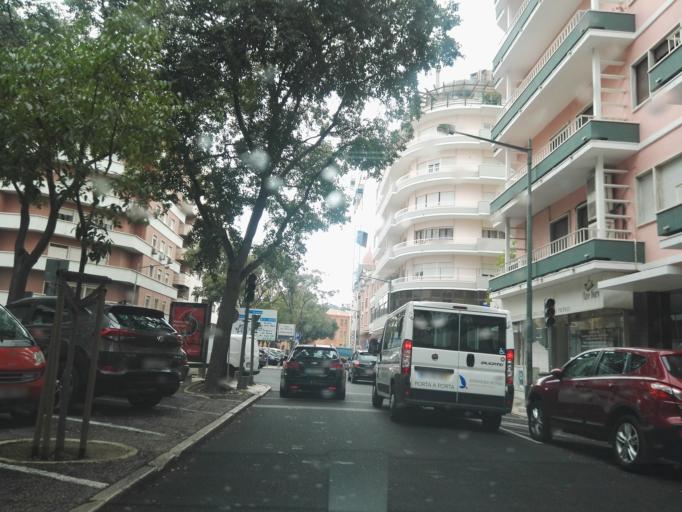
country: PT
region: Lisbon
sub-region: Lisbon
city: Lisbon
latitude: 38.7402
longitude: -9.1445
